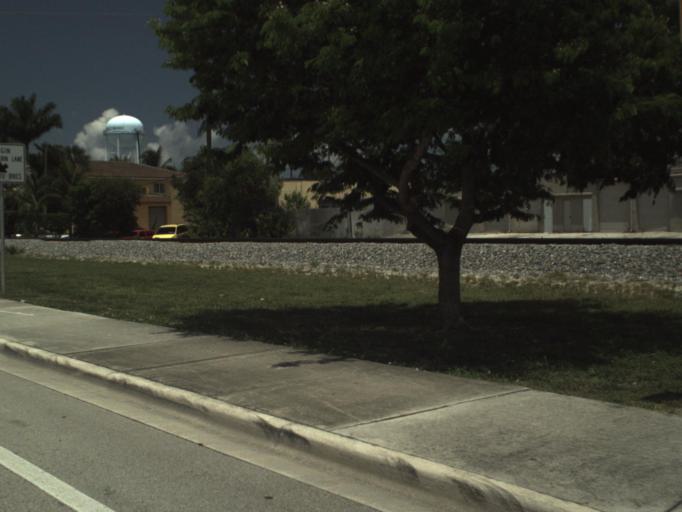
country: US
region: Florida
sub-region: Broward County
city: Deerfield Beach
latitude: 26.3037
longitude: -80.1056
